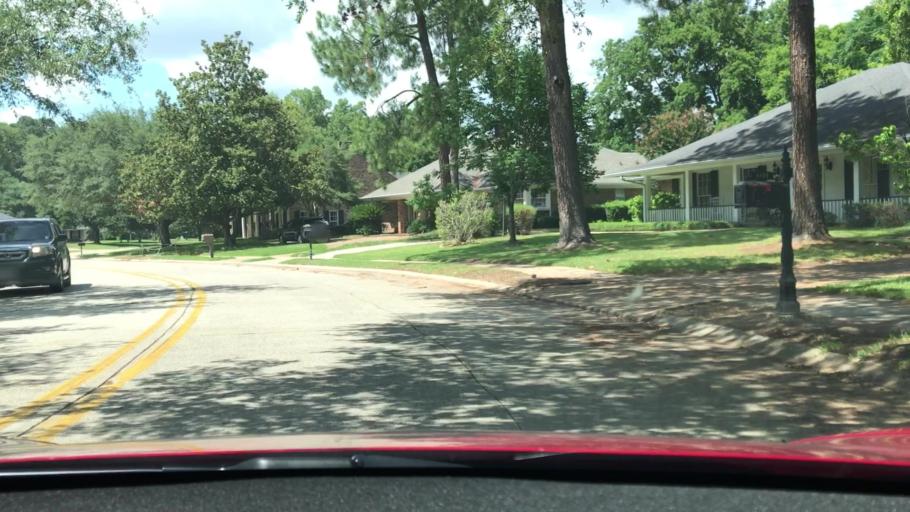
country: US
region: Louisiana
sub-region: Bossier Parish
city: Bossier City
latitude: 32.4262
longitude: -93.7276
